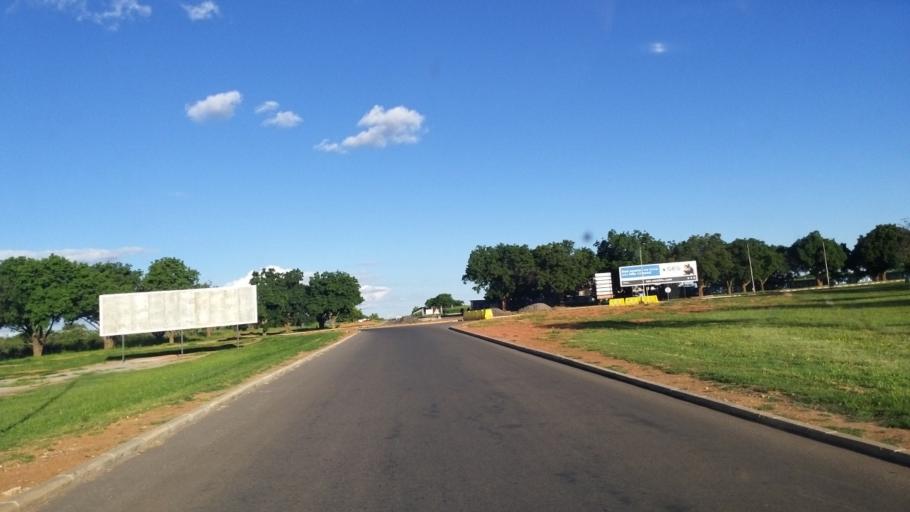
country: ZM
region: Lusaka
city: Lusaka
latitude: -15.3205
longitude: 28.4462
